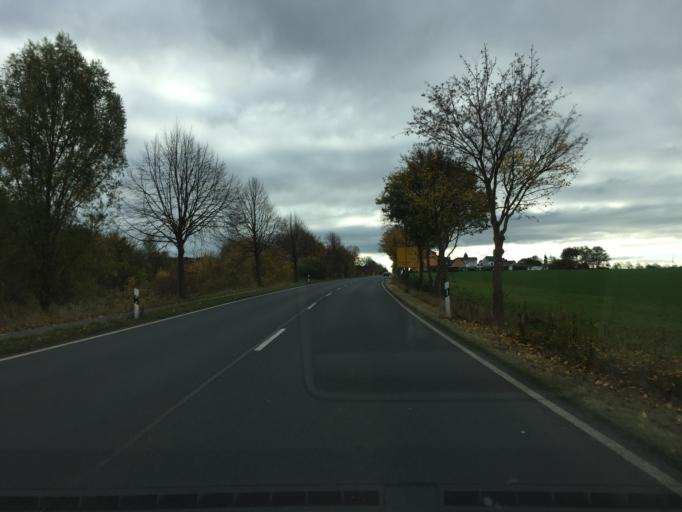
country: DE
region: Lower Saxony
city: Leiferde
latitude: 52.2037
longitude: 10.4949
